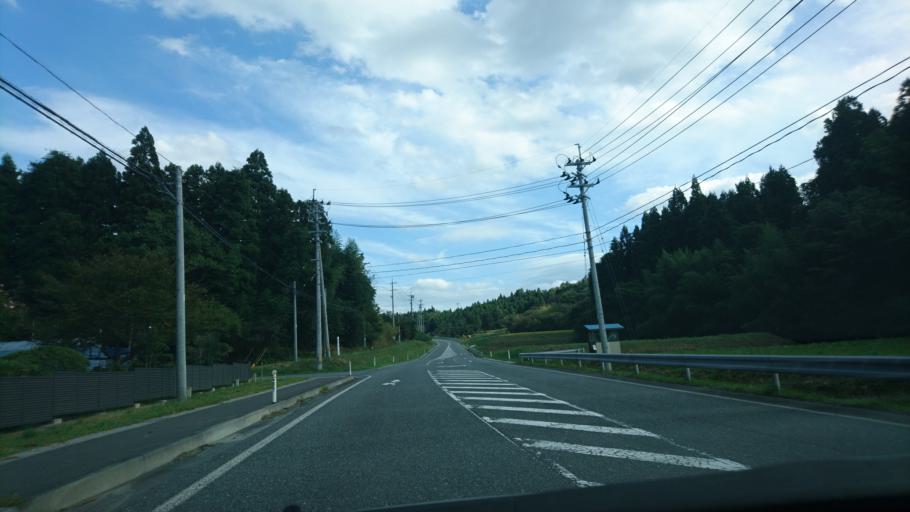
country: JP
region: Iwate
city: Ichinoseki
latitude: 38.8333
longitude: 141.2174
